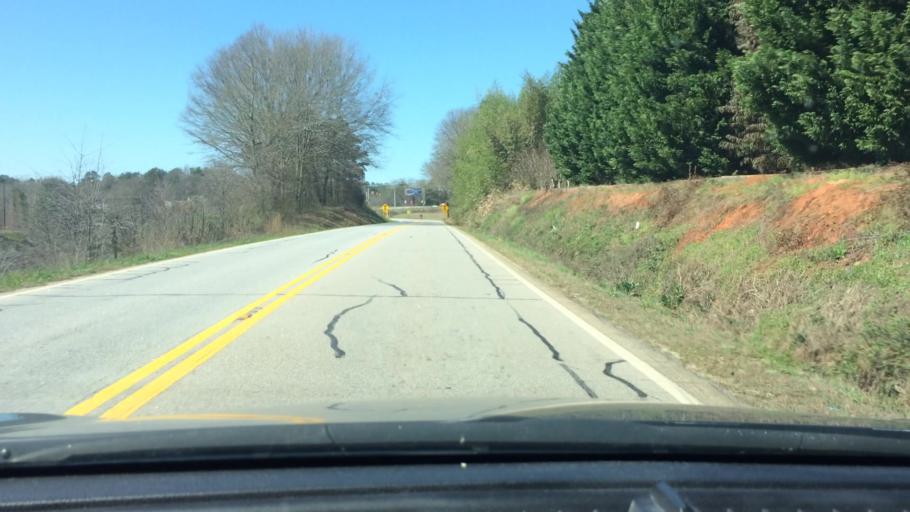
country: US
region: South Carolina
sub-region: Oconee County
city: Utica
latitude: 34.7130
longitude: -82.9202
